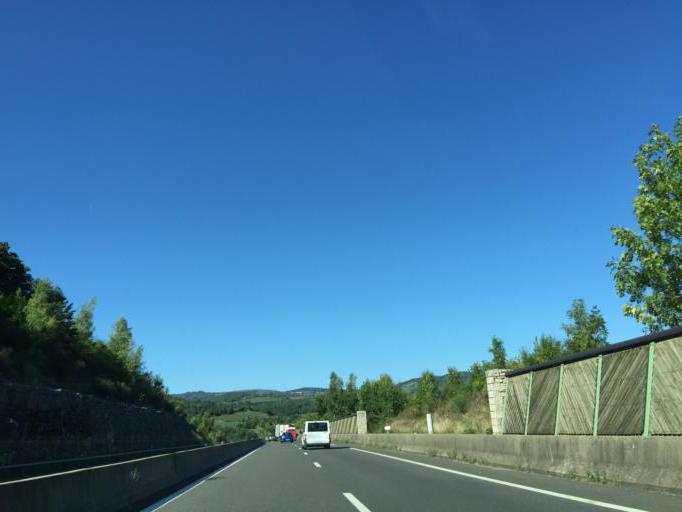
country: FR
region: Languedoc-Roussillon
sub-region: Departement de la Lozere
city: La Canourgue
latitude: 44.4563
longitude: 3.1914
